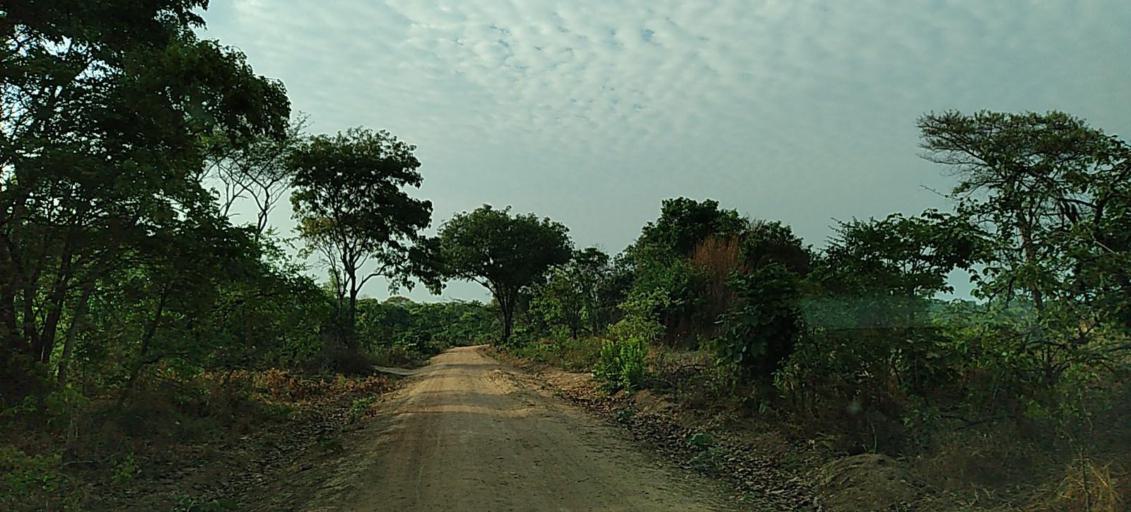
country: ZM
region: Copperbelt
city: Chingola
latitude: -12.8748
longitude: 27.6907
